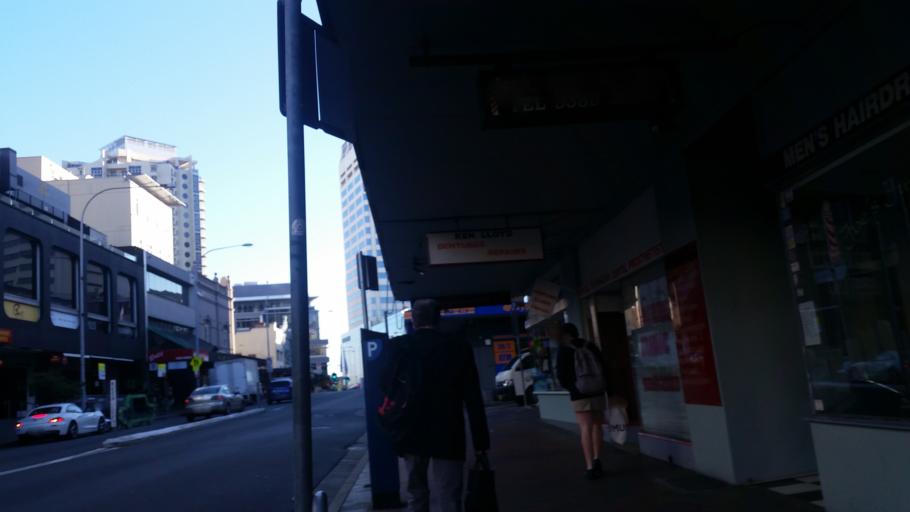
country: AU
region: New South Wales
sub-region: Waverley
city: Bondi Junction
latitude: -33.8935
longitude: 151.2495
